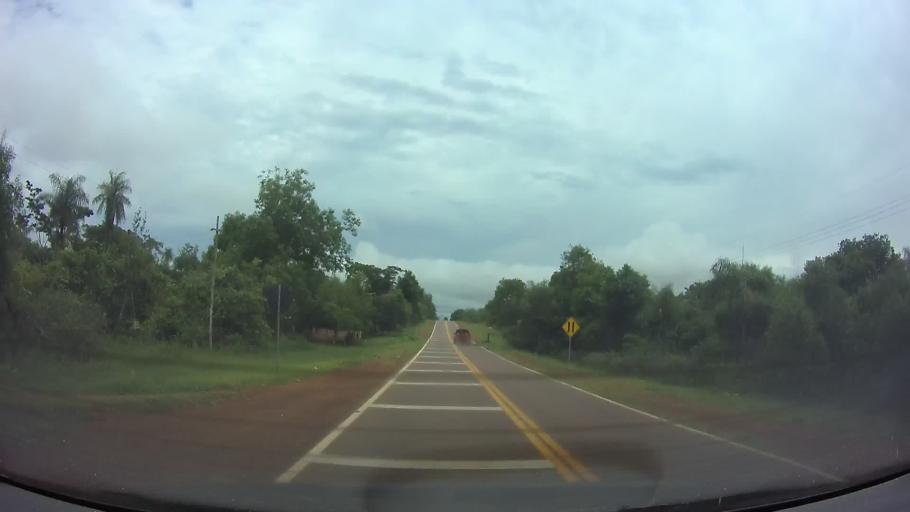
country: PY
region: Paraguari
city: Acahay
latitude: -25.8592
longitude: -57.1339
